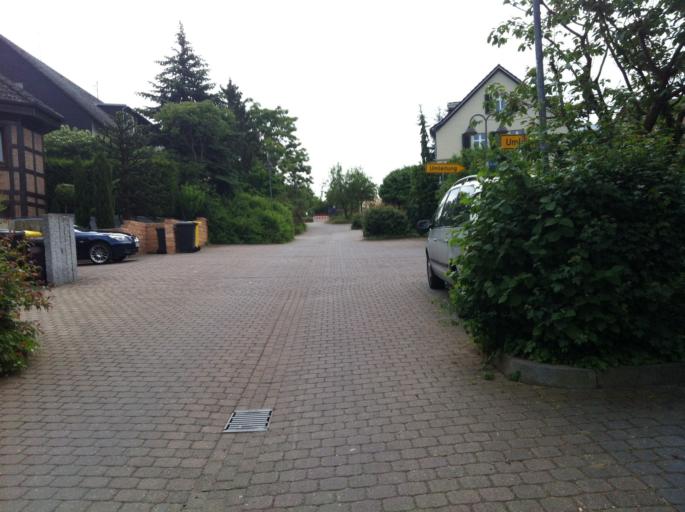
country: DE
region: Rheinland-Pfalz
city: Budenheim
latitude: 50.0217
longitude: 8.1773
